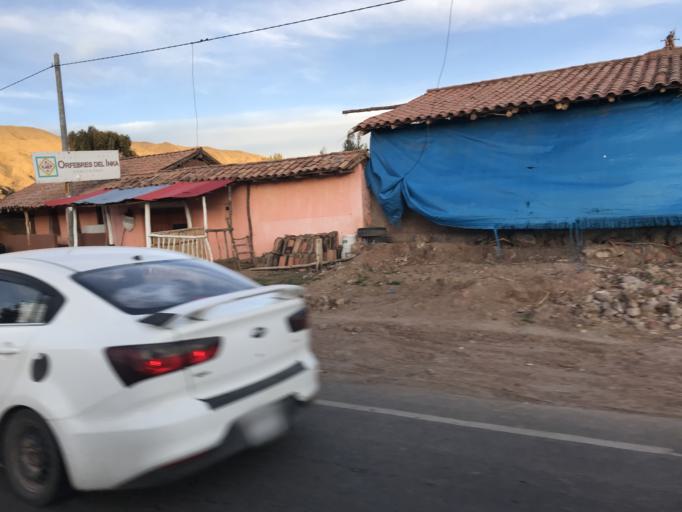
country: PE
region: Cusco
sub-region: Provincia de Cusco
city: Cusco
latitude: -13.4892
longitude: -71.9644
